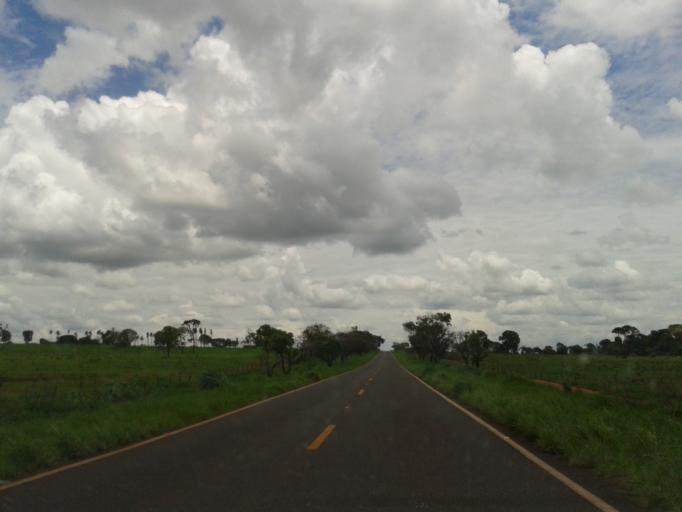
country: BR
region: Minas Gerais
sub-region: Ituiutaba
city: Ituiutaba
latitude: -19.0556
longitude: -49.7667
